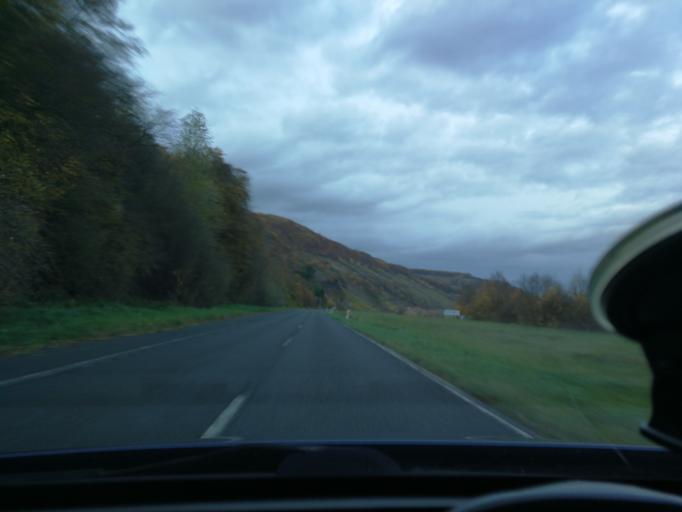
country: DE
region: Rheinland-Pfalz
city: Wintrich
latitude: 49.8780
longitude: 6.9455
